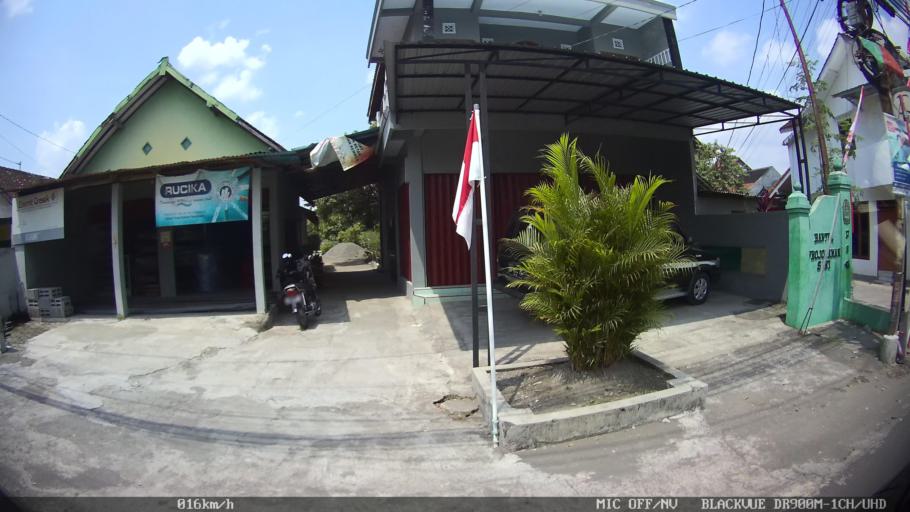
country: ID
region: Daerah Istimewa Yogyakarta
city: Yogyakarta
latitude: -7.8256
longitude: 110.4074
